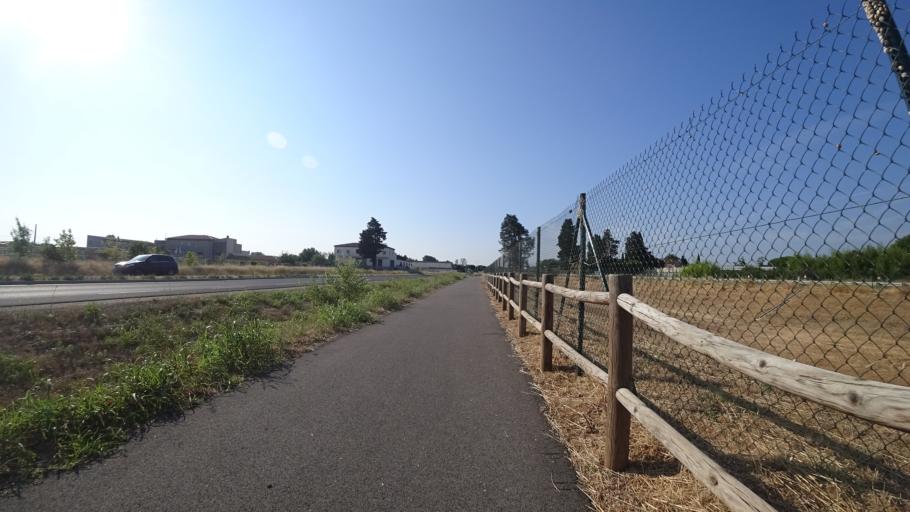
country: FR
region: Languedoc-Roussillon
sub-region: Departement des Pyrenees-Orientales
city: Perpignan
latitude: 42.7125
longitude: 2.9063
